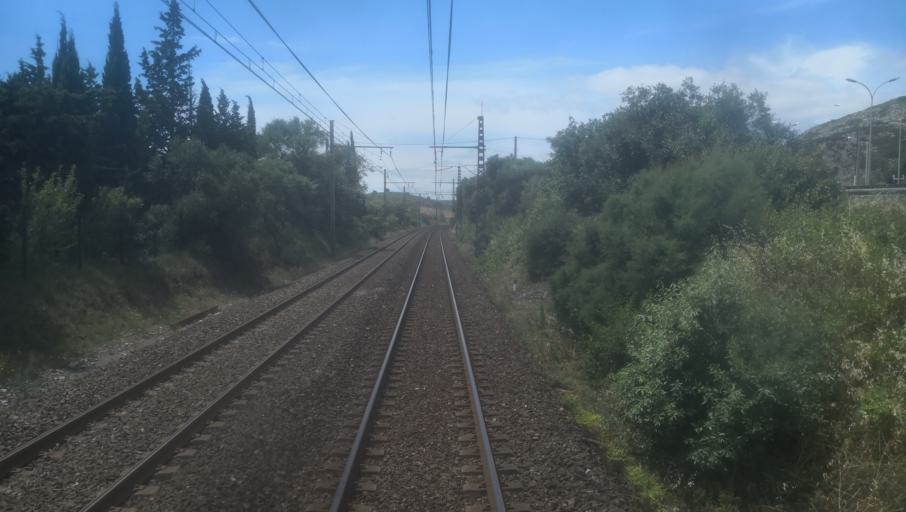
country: FR
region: Languedoc-Roussillon
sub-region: Departement de l'Aude
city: Narbonne
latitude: 43.1802
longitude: 2.9625
